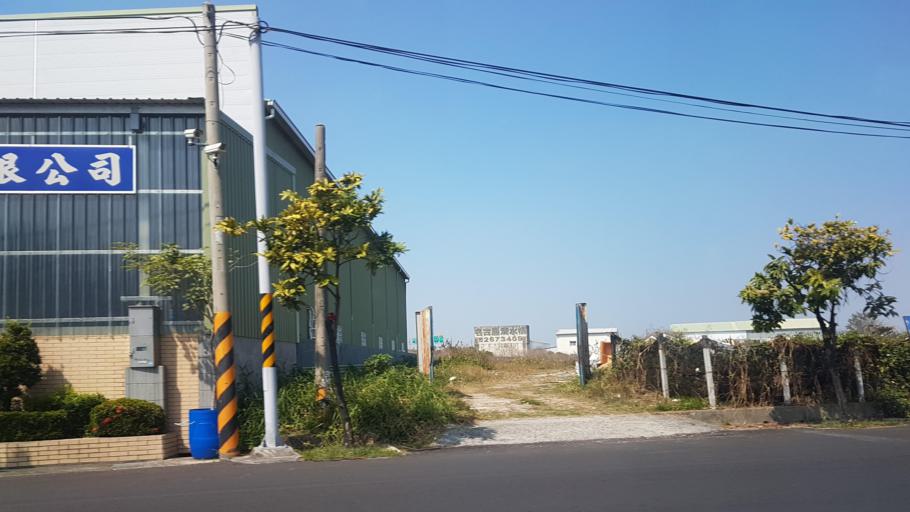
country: TW
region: Taiwan
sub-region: Tainan
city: Tainan
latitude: 22.9348
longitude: 120.2538
